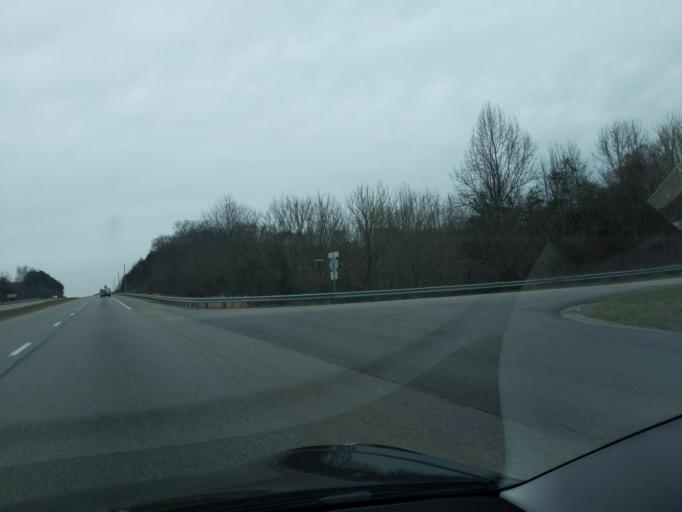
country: US
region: Kentucky
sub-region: Bell County
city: Pineville
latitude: 36.8348
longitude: -83.7802
